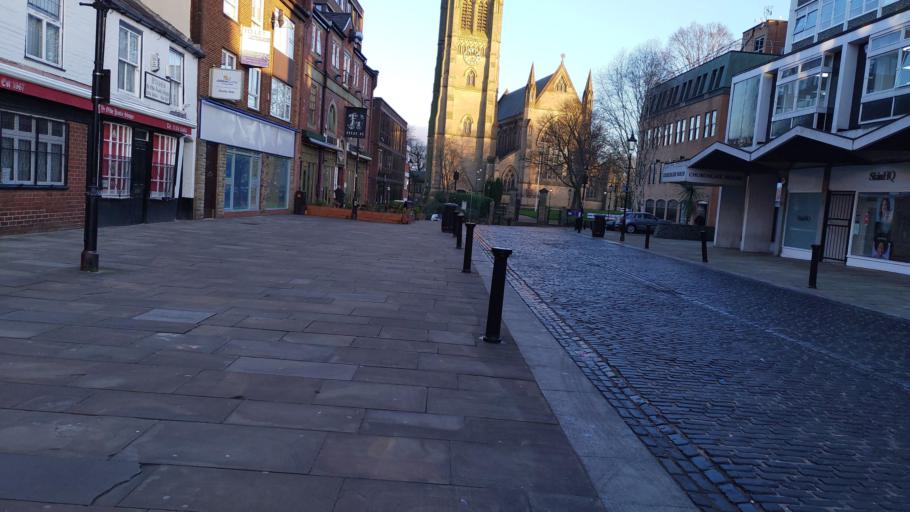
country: GB
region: England
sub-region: Borough of Bolton
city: Bolton
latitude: 53.5797
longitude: -2.4259
